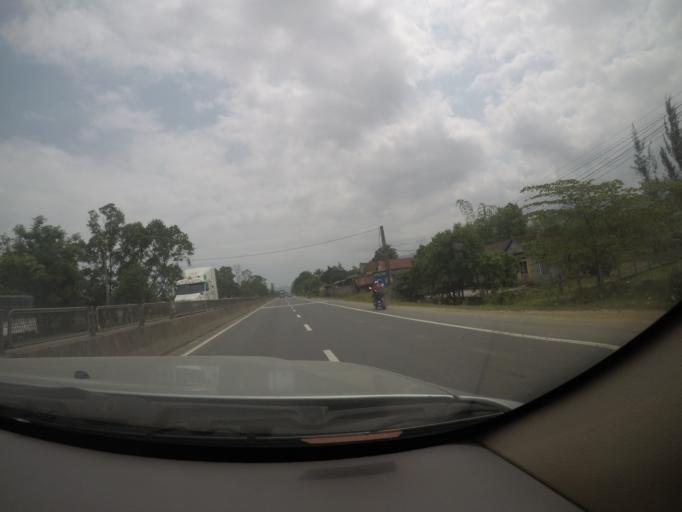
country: VN
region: Thua Thien-Hue
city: Phu Loc
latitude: 16.2724
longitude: 107.9483
